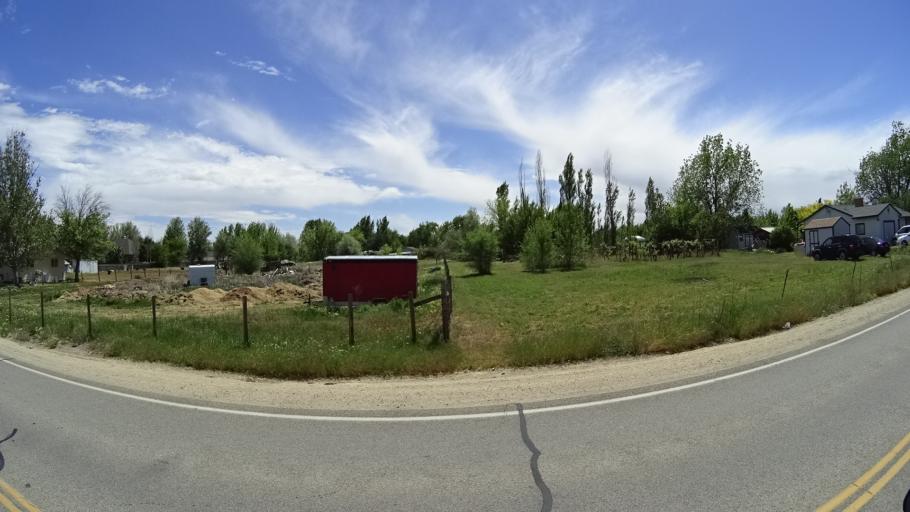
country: US
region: Idaho
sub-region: Ada County
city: Meridian
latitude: 43.5757
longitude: -116.3301
